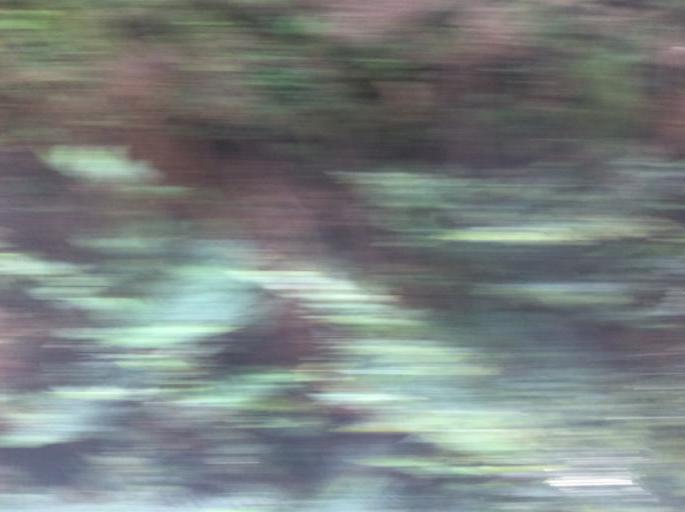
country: TW
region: Taipei
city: Taipei
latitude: 25.1526
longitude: 121.5437
